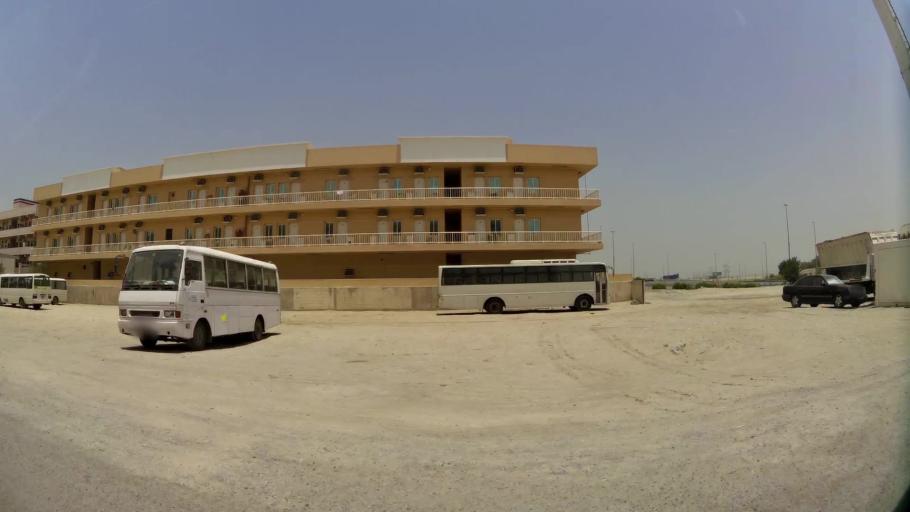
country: AE
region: Ash Shariqah
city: Sharjah
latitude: 25.2766
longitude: 55.4252
